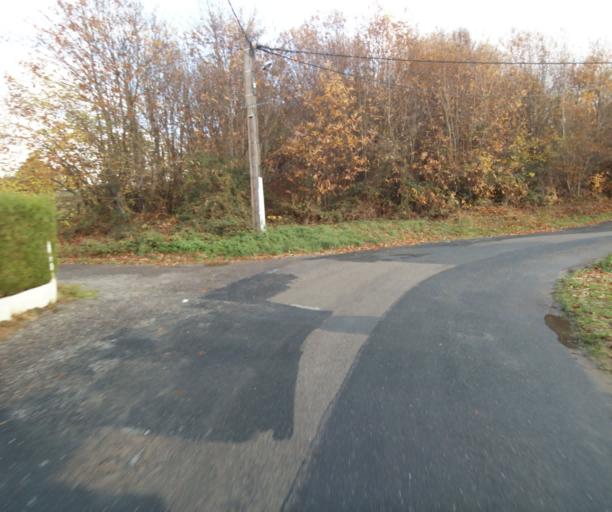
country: FR
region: Limousin
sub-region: Departement de la Correze
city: Cornil
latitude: 45.2186
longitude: 1.6735
